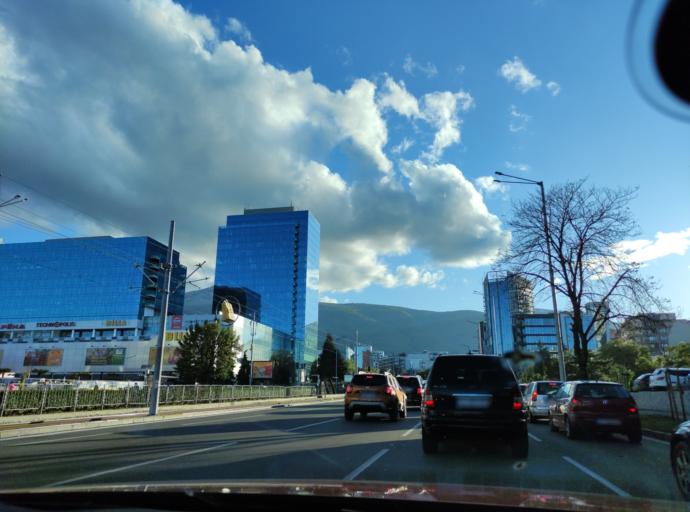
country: BG
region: Sofia-Capital
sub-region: Stolichna Obshtina
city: Sofia
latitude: 42.6663
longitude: 23.2890
